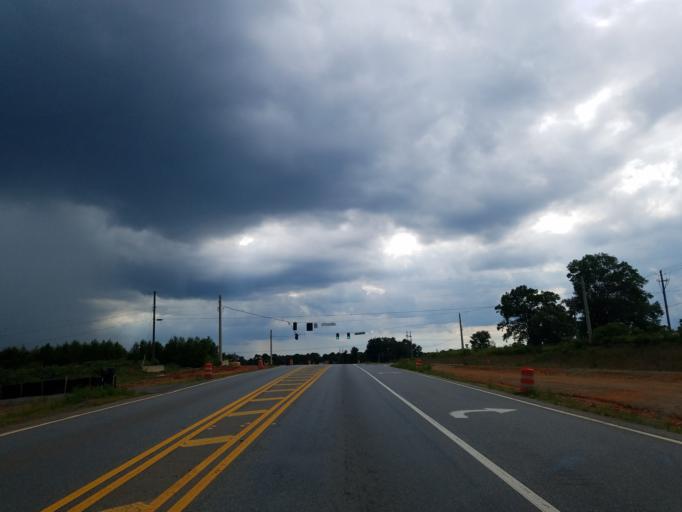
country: US
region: Georgia
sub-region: Floyd County
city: Shannon
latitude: 34.3675
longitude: -85.0393
